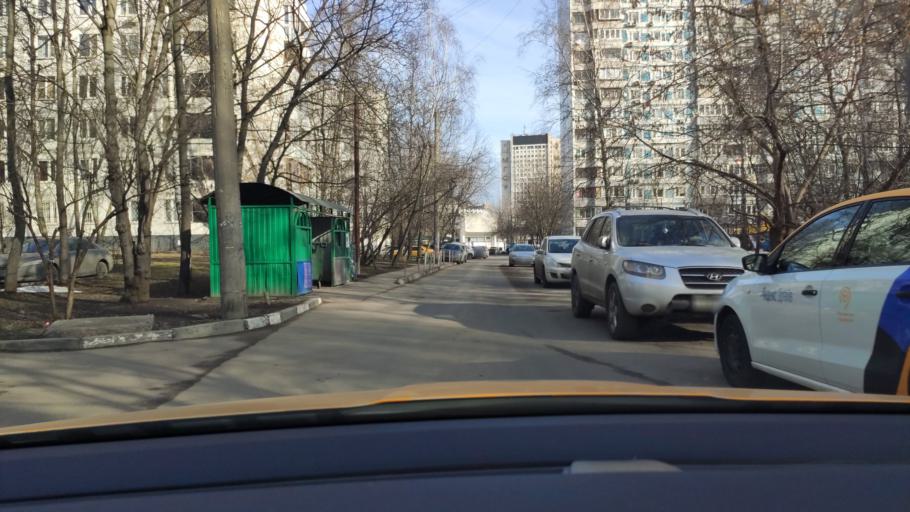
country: RU
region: Moscow
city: Vatutino
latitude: 55.8552
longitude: 37.6872
